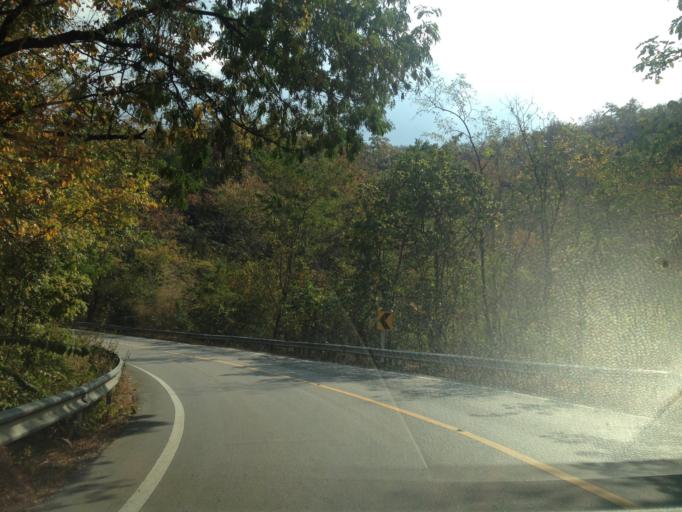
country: TH
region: Chiang Mai
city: Hot
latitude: 18.2250
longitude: 98.4898
